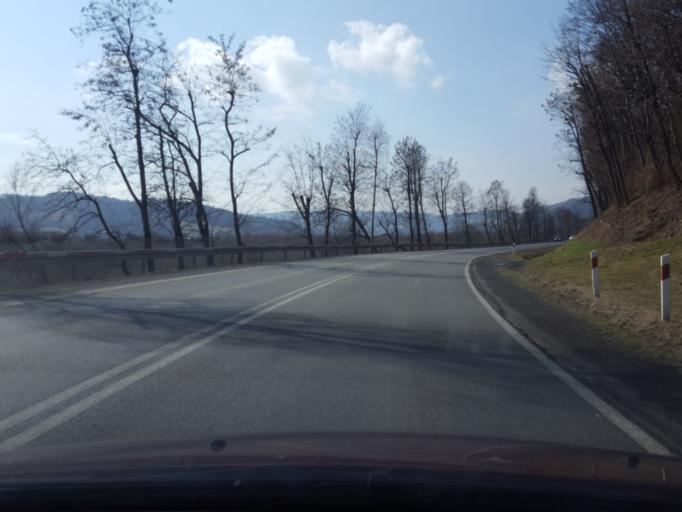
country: PL
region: Lesser Poland Voivodeship
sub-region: Powiat nowosadecki
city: Lososina Dolna
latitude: 49.6958
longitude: 20.6602
